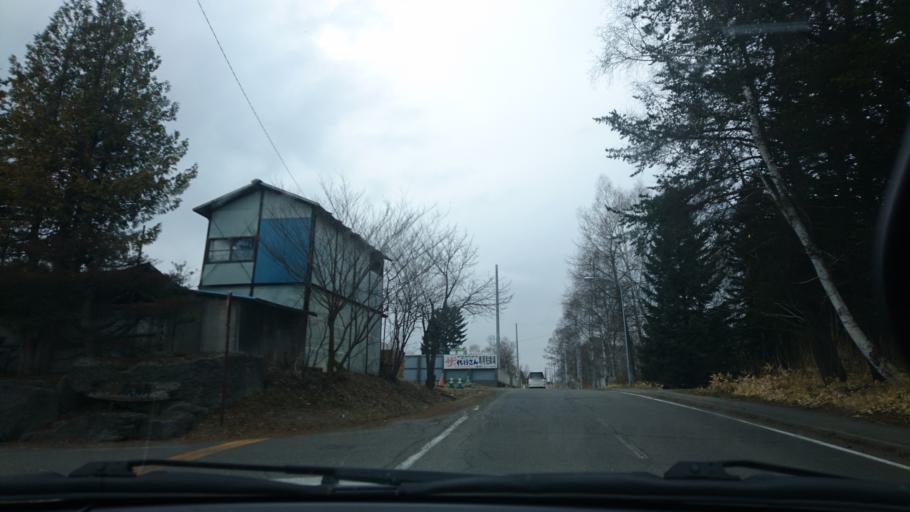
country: JP
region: Hokkaido
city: Otofuke
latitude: 42.9721
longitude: 143.2024
